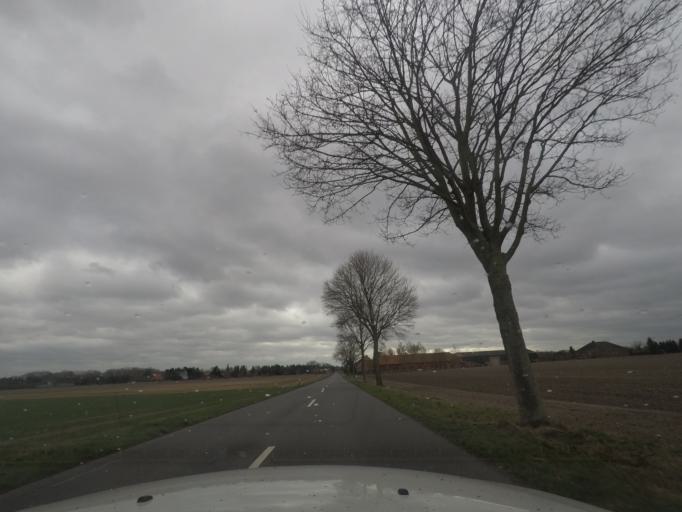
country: DE
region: Lower Saxony
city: Emmendorf
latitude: 53.0112
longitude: 10.6011
